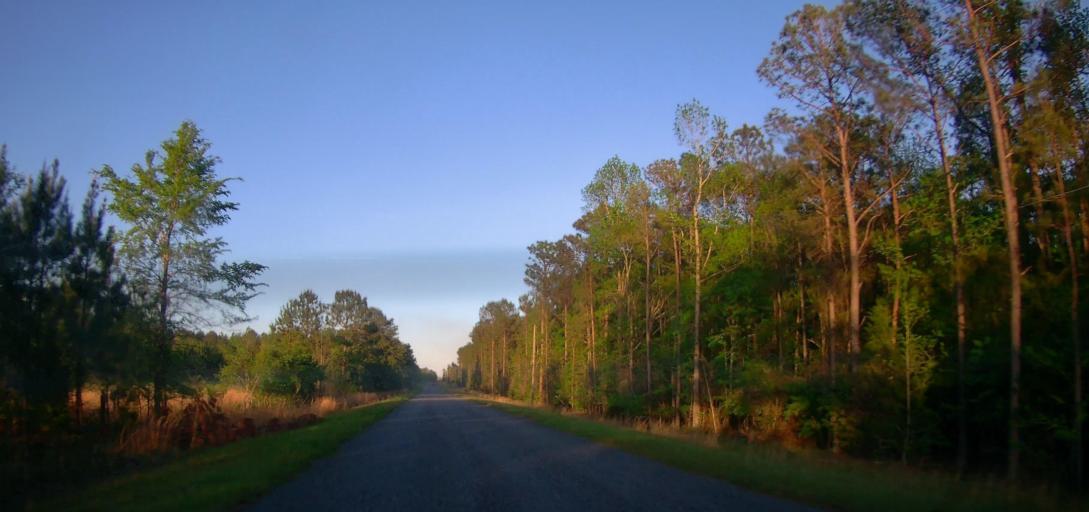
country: US
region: Georgia
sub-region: Talbot County
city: Talbotton
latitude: 32.5364
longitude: -84.5902
